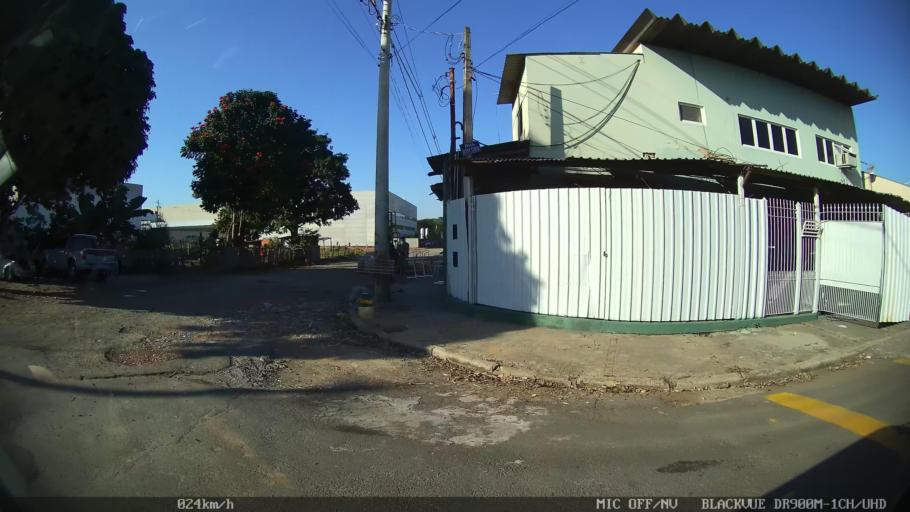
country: BR
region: Sao Paulo
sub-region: Nova Odessa
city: Nova Odessa
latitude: -22.7705
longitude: -47.2902
